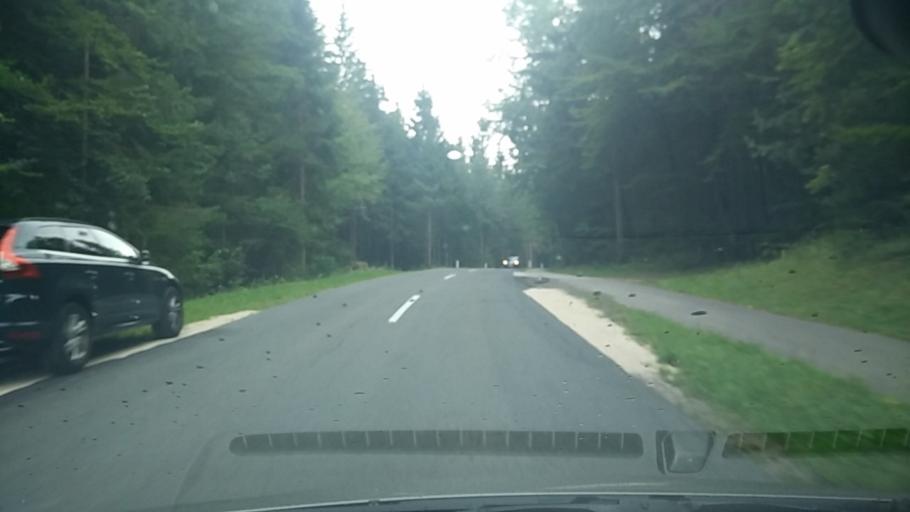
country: AT
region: Carinthia
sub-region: Politischer Bezirk Volkermarkt
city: Sittersdorf
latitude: 46.5986
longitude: 14.5696
